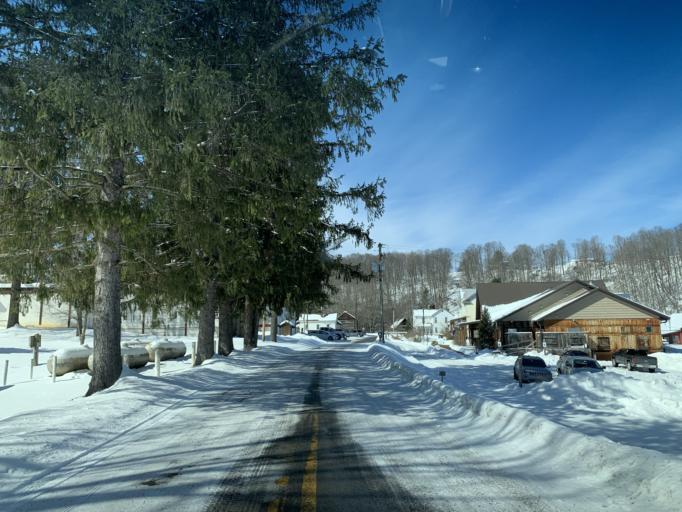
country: US
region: Pennsylvania
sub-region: Somerset County
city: Meyersdale
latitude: 39.6965
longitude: -79.1403
